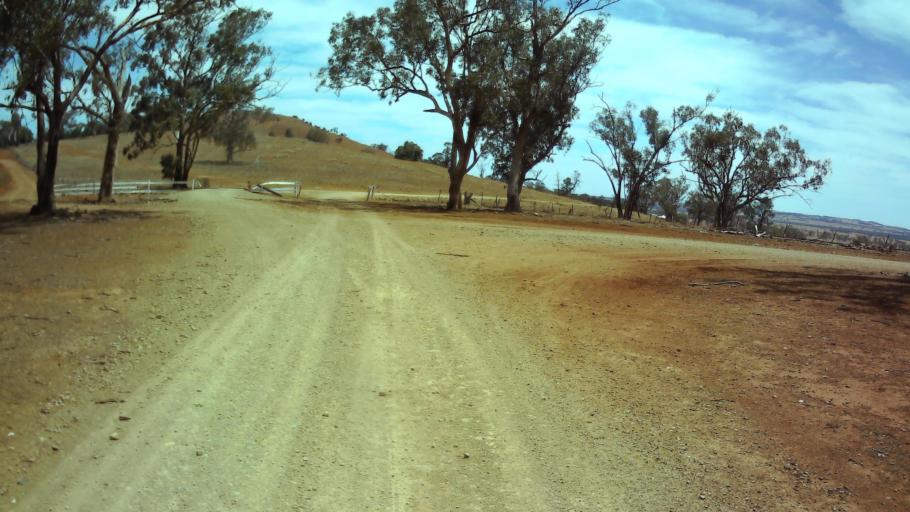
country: AU
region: New South Wales
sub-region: Weddin
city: Grenfell
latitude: -33.7472
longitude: 148.1690
